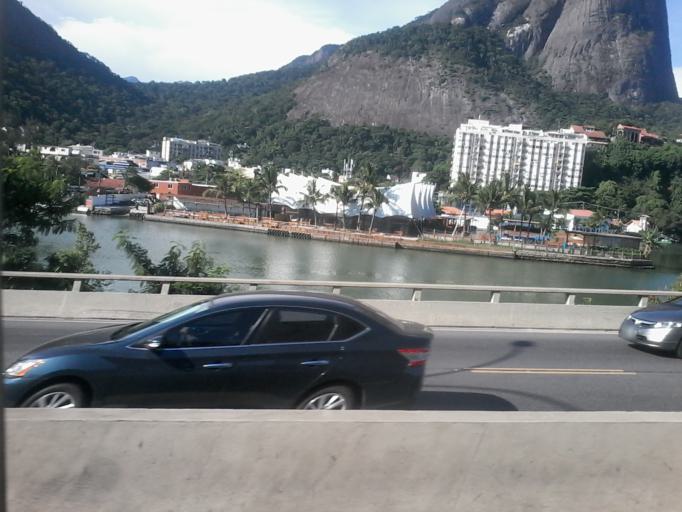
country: BR
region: Rio de Janeiro
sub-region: Rio De Janeiro
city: Rio de Janeiro
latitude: -23.0131
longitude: -43.2981
